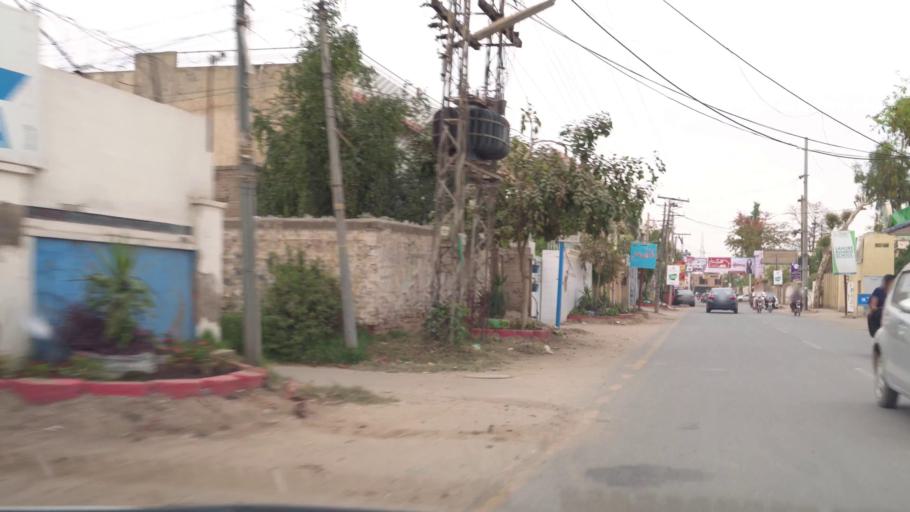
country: PK
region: Punjab
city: Sargodha
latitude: 32.0763
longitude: 72.6787
